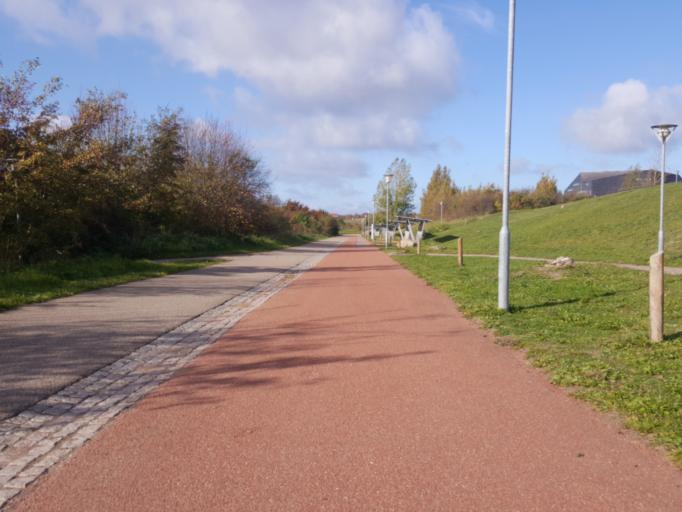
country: DK
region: Zealand
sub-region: Kalundborg Kommune
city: Kalundborg
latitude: 55.6913
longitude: 11.0838
